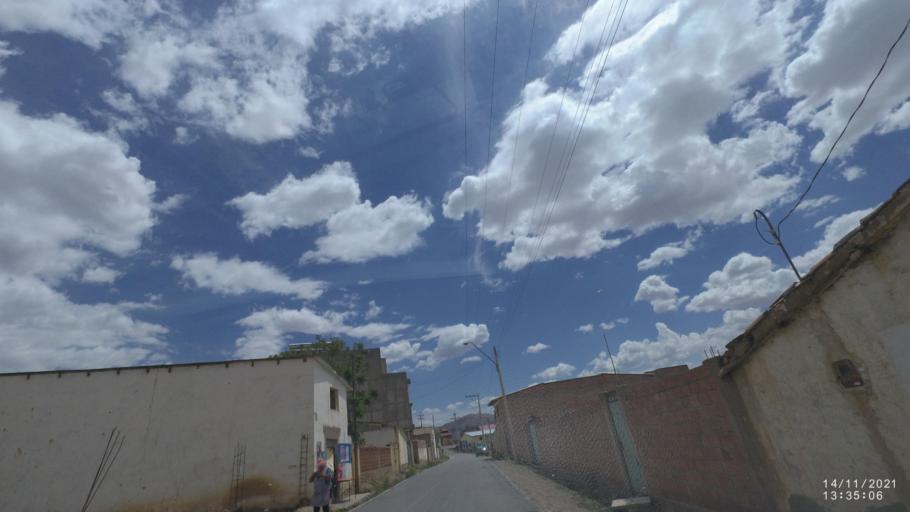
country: BO
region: Cochabamba
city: Colomi
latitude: -17.4063
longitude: -65.9865
